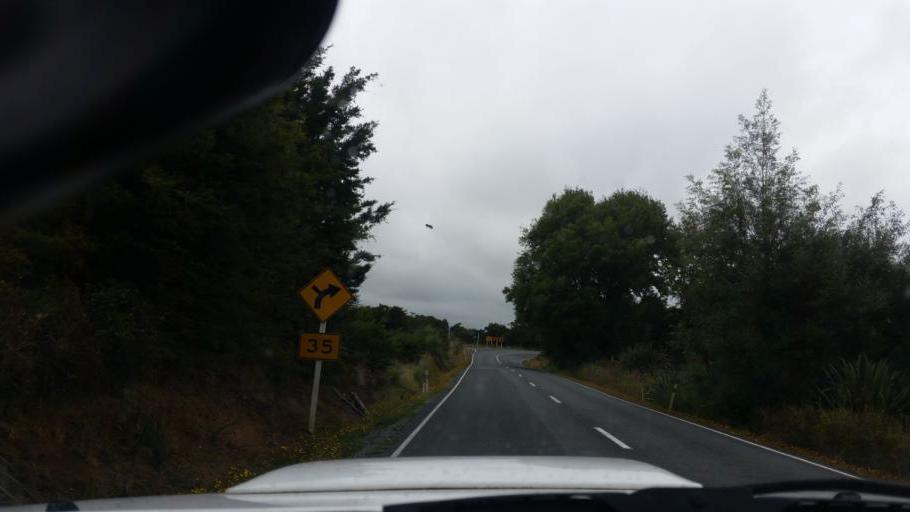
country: NZ
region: Auckland
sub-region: Auckland
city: Wellsford
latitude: -36.1395
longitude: 174.5066
